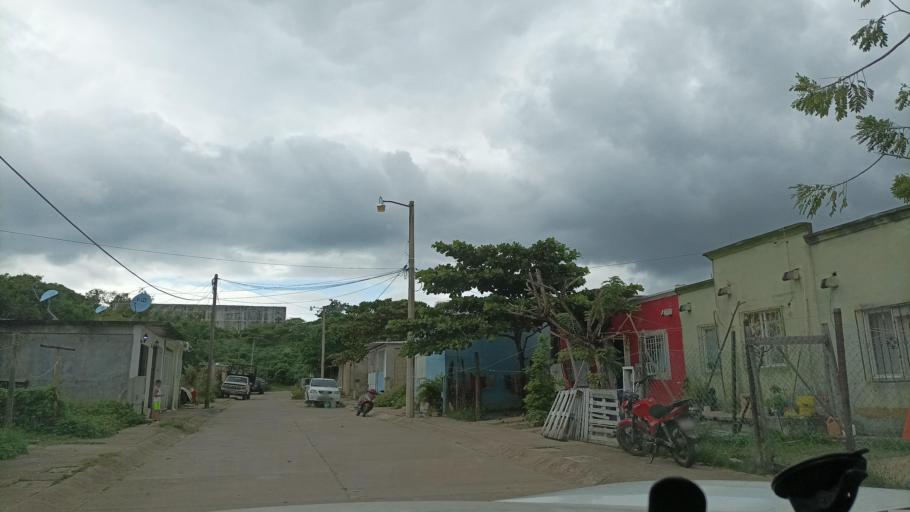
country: MX
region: Veracruz
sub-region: Soconusco
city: Fraccionamiento Santa Cruz
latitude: 17.9712
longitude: -94.8976
